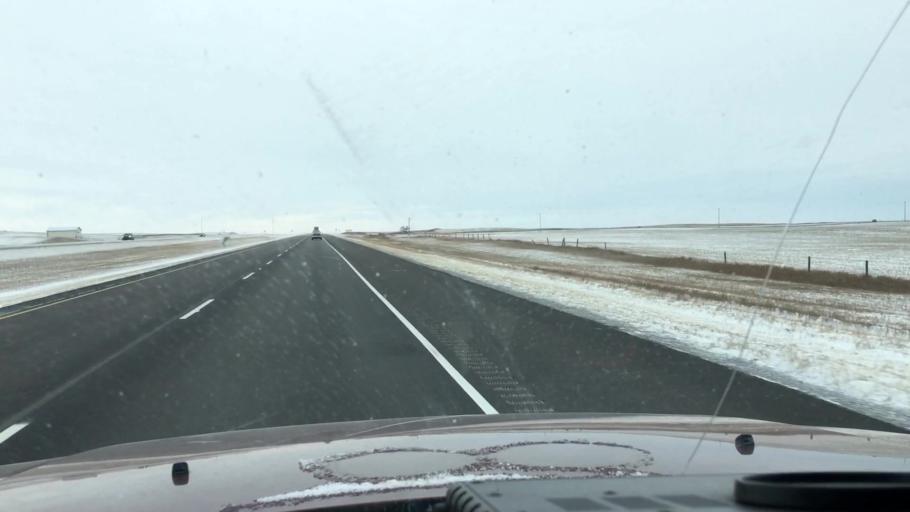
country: CA
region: Saskatchewan
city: Saskatoon
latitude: 51.7114
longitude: -106.4658
